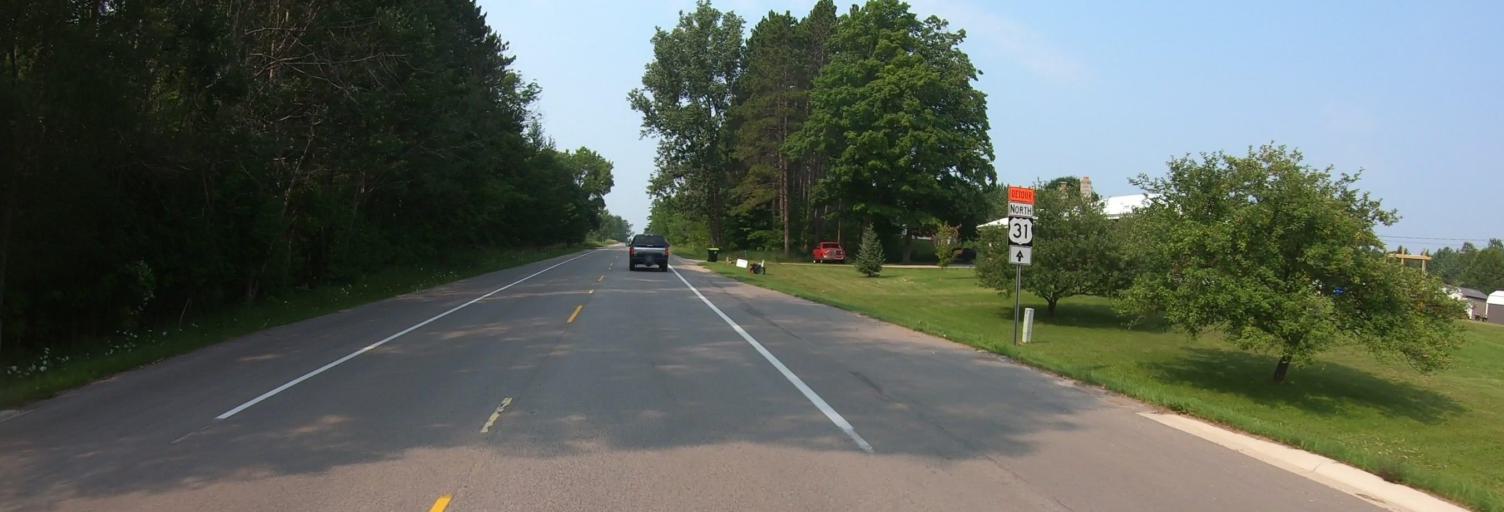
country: US
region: Michigan
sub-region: Charlevoix County
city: Charlevoix
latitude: 45.2213
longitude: -85.2614
